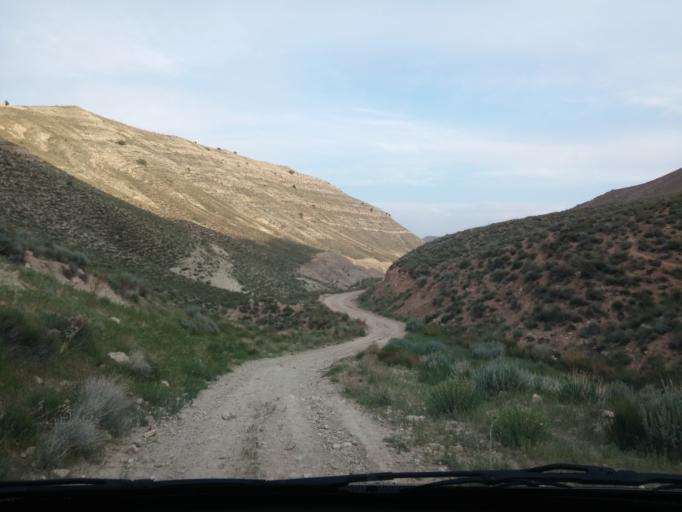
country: IR
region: Semnan
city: Istgah-e Rah Ahan-e Garmsar
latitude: 35.4839
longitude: 52.2923
